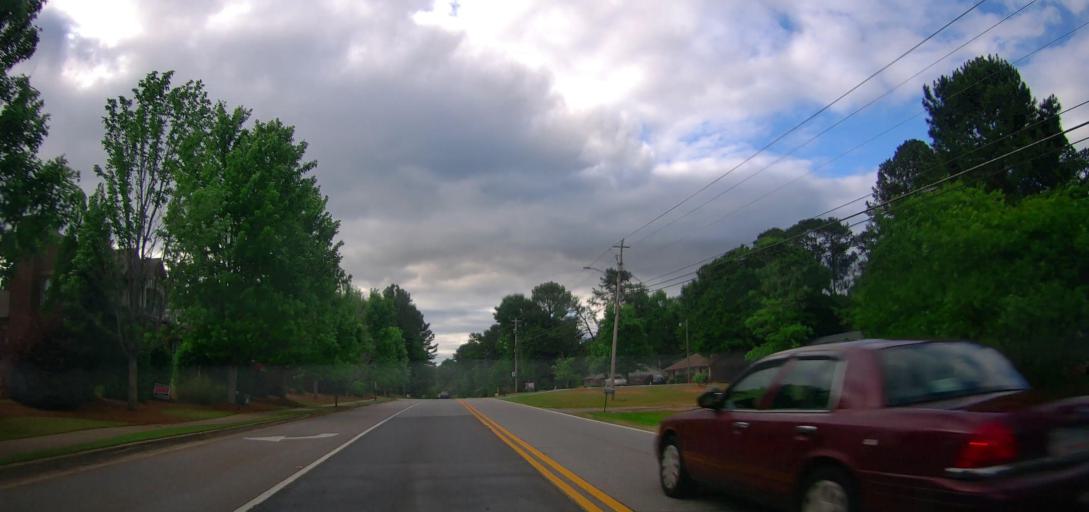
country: US
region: Georgia
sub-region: Clarke County
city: Athens
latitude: 33.9249
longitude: -83.4108
